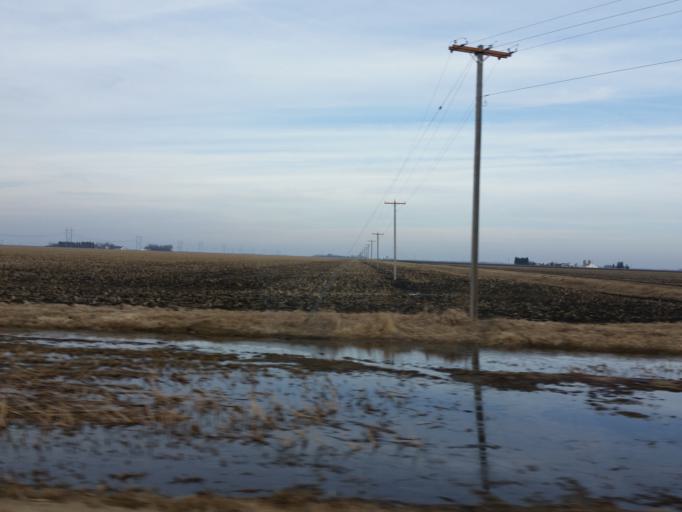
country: US
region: North Dakota
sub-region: Cass County
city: Casselton
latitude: 46.9490
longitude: -97.2198
